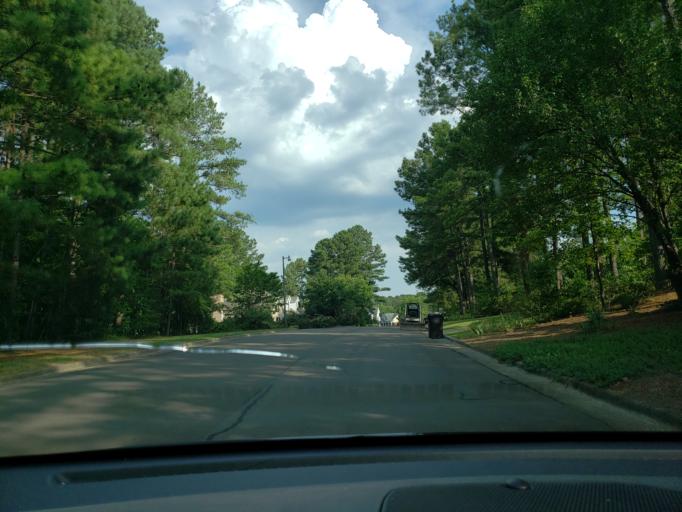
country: US
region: North Carolina
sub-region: Orange County
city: Chapel Hill
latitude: 35.9070
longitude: -78.9853
